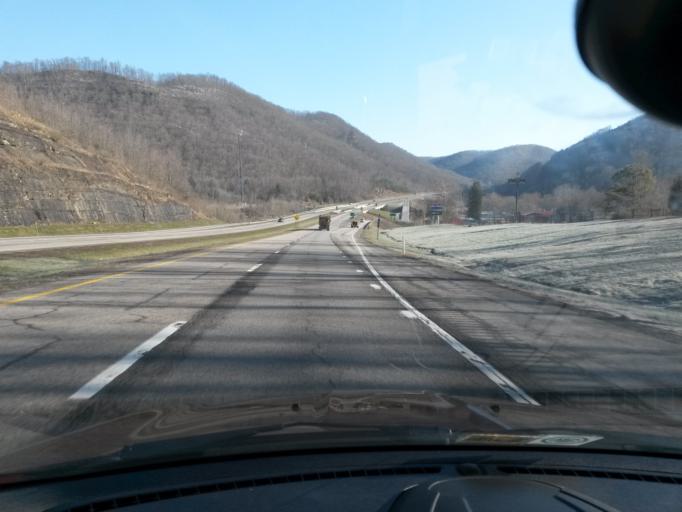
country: US
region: West Virginia
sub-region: Braxton County
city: Sutton
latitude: 38.4958
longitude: -80.7578
